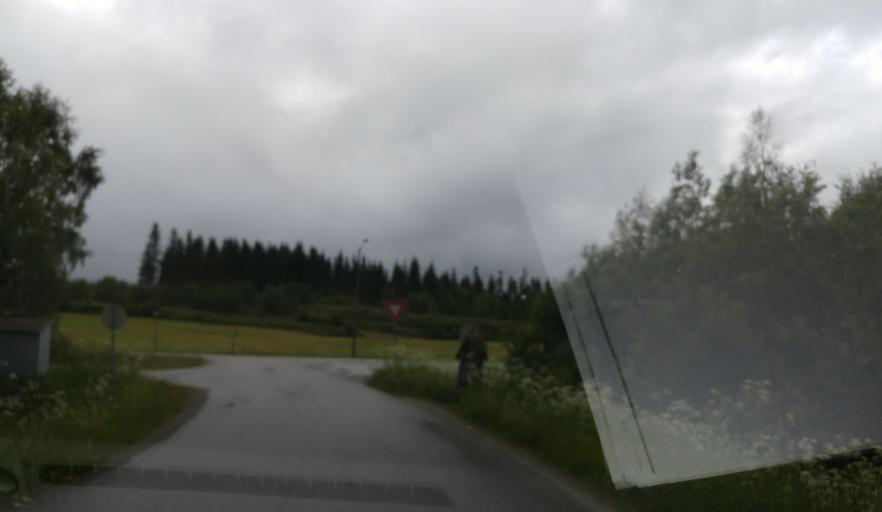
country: NO
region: Sor-Trondelag
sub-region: Selbu
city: Mebonden
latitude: 63.2610
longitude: 11.0829
